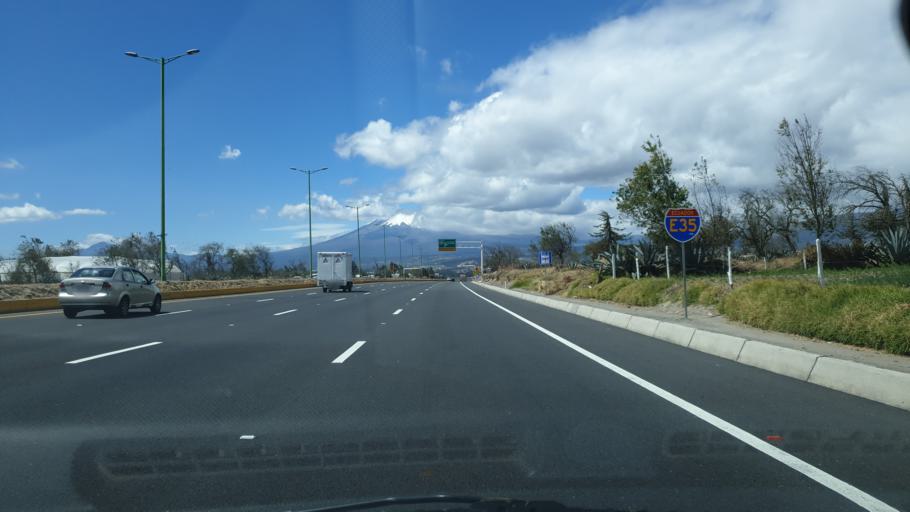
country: EC
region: Cotopaxi
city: Saquisili
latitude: -0.8804
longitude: -78.6502
